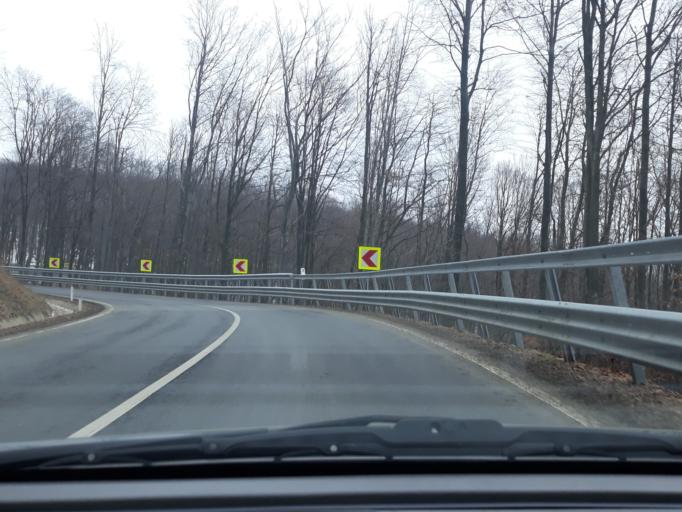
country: RO
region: Bihor
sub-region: Oras Alesd
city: Padurea Neagra
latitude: 47.1216
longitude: 22.4236
